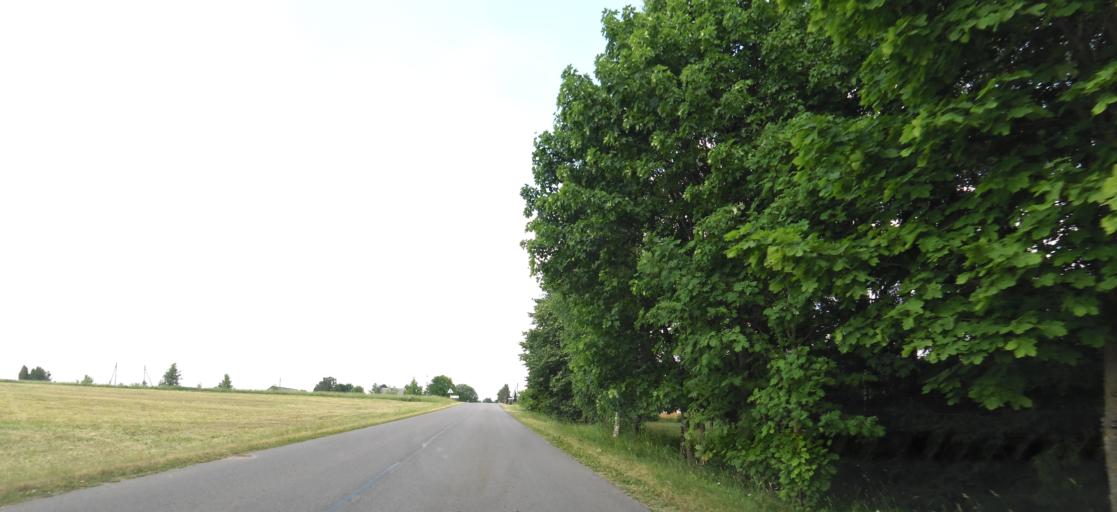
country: LT
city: Skaidiskes
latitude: 54.5303
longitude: 25.6403
